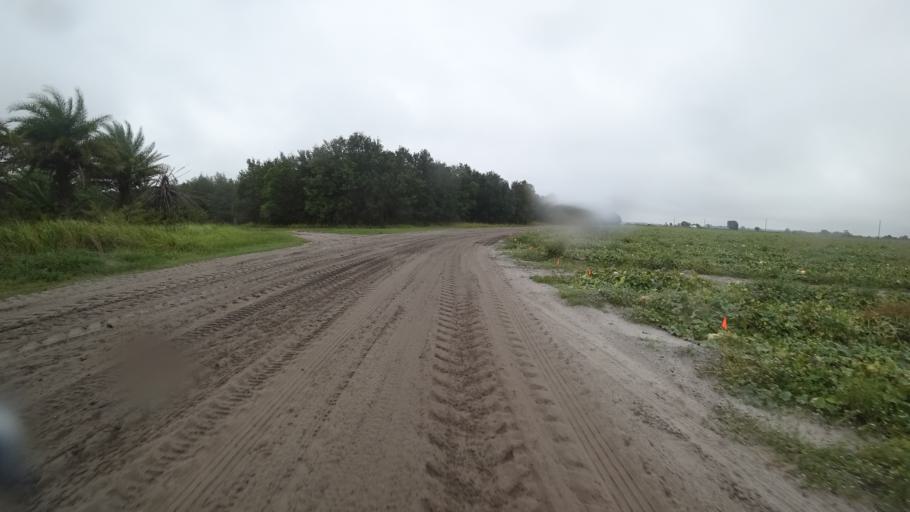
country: US
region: Florida
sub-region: Sarasota County
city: Warm Mineral Springs
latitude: 27.2810
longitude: -82.1718
